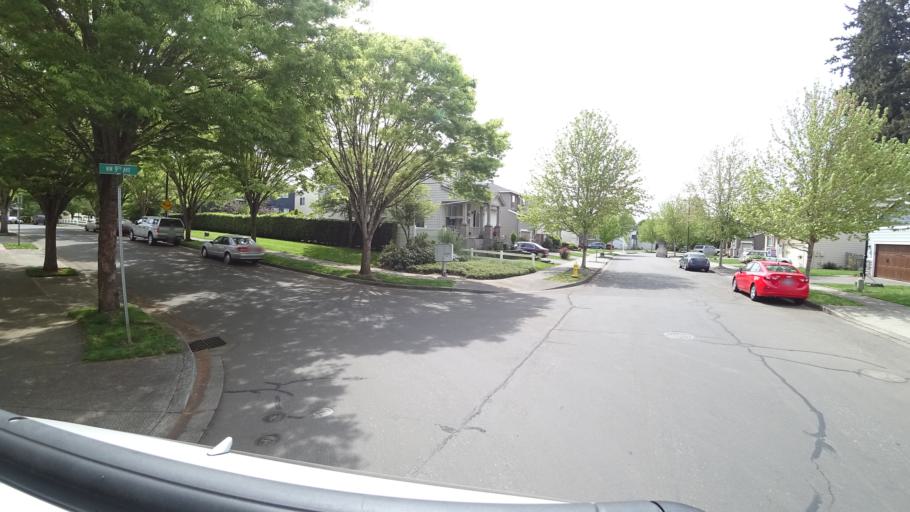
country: US
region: Oregon
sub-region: Washington County
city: Hillsboro
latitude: 45.5379
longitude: -122.9985
